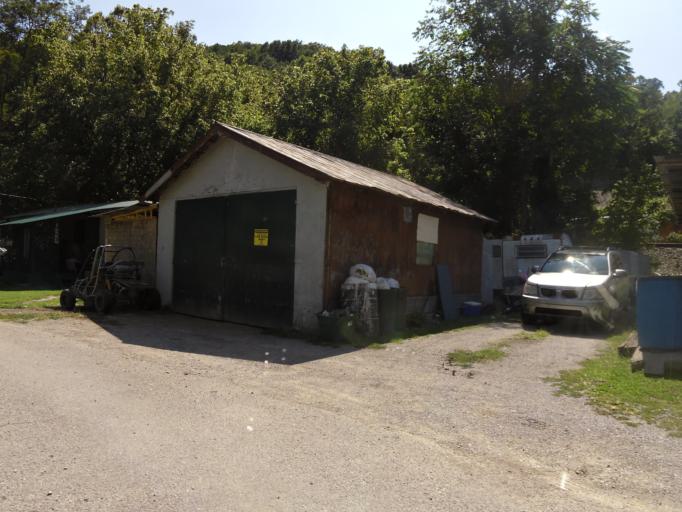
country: US
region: Kentucky
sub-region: Harlan County
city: Harlan
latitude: 36.8049
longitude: -83.3040
